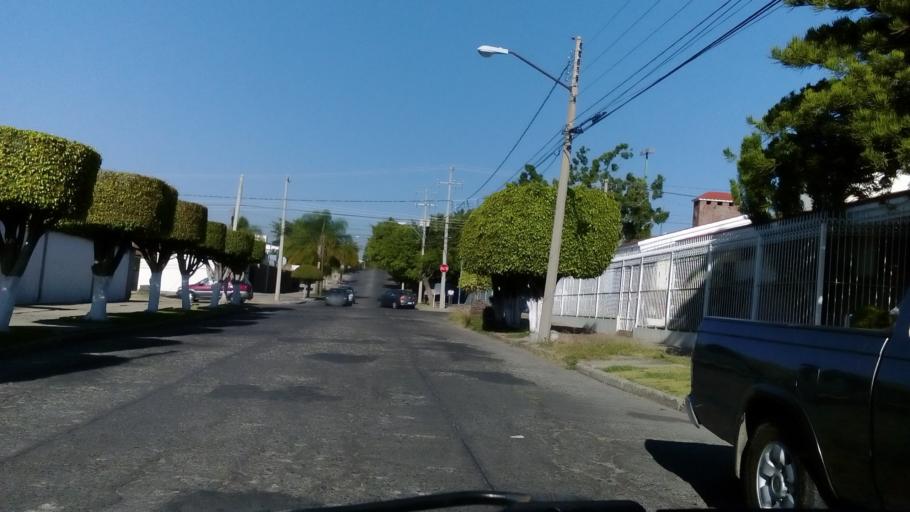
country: MX
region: Guanajuato
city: Leon
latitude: 21.1212
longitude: -101.6974
